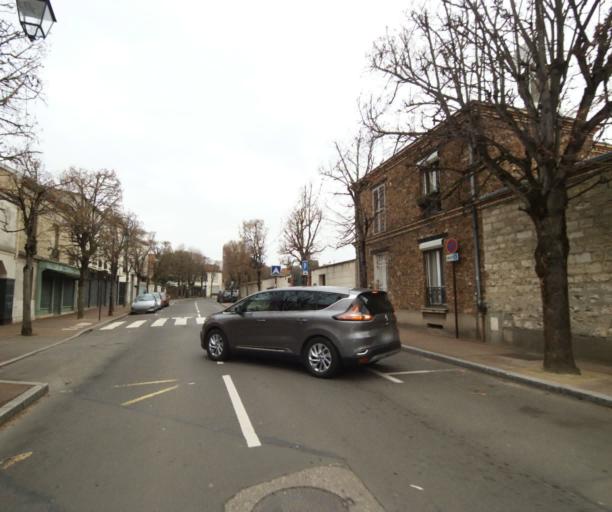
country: FR
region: Ile-de-France
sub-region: Departement des Hauts-de-Seine
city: Saint-Cloud
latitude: 48.8479
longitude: 2.2052
